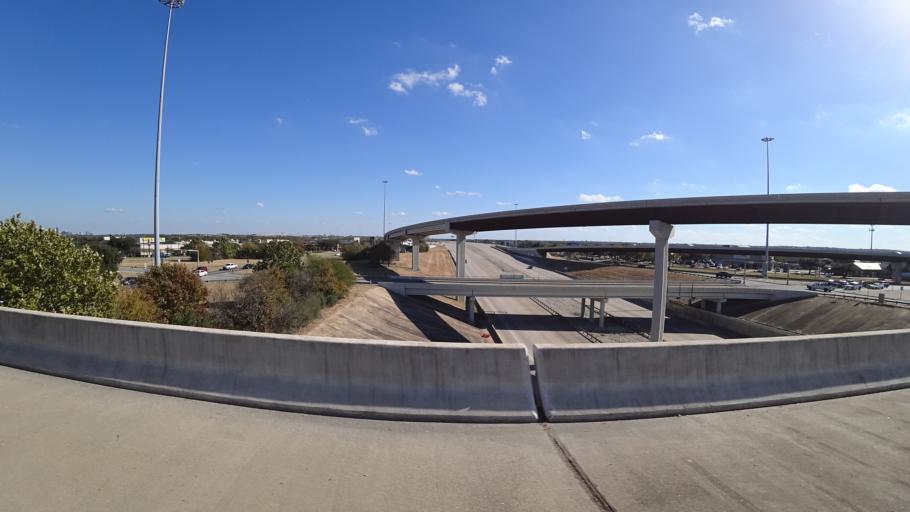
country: US
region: Texas
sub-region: Travis County
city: Rollingwood
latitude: 30.2355
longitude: -97.8244
